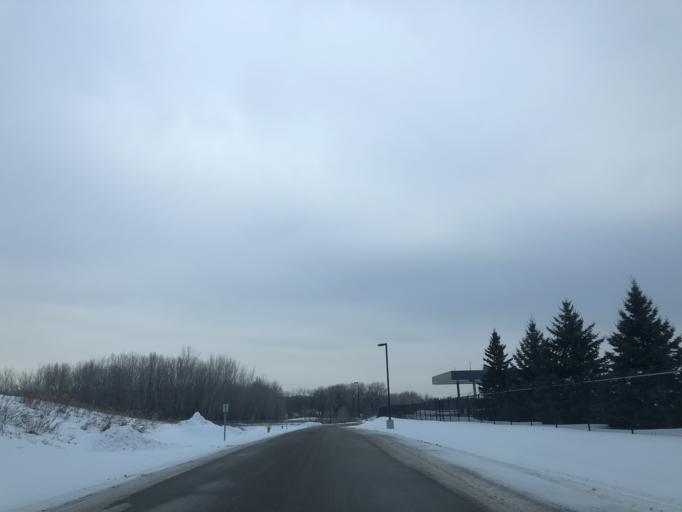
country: US
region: Minnesota
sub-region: Ramsey County
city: Shoreview
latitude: 45.0820
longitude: -93.1638
